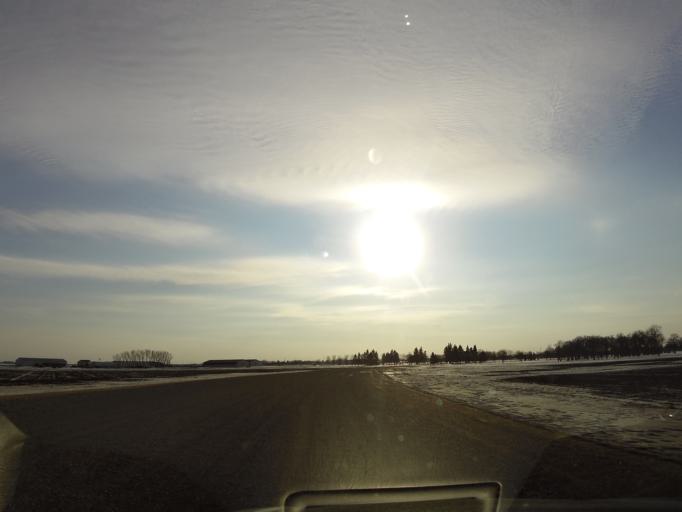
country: US
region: North Dakota
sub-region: Walsh County
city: Grafton
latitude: 48.4186
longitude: -97.3820
